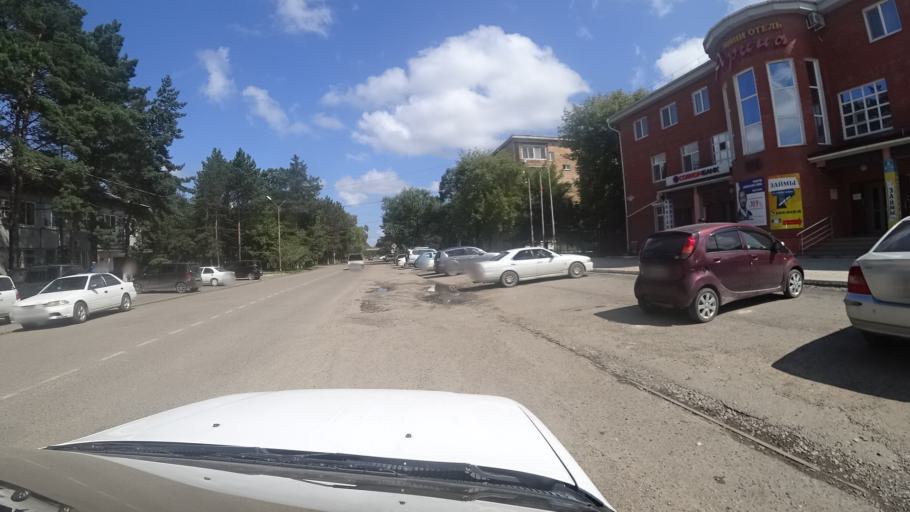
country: RU
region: Primorskiy
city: Dal'nerechensk
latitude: 45.9339
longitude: 133.7358
